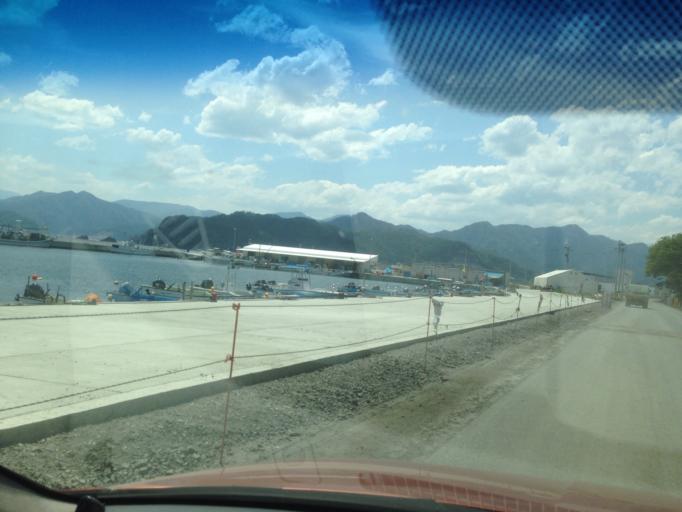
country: JP
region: Iwate
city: Otsuchi
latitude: 39.3532
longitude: 141.9302
